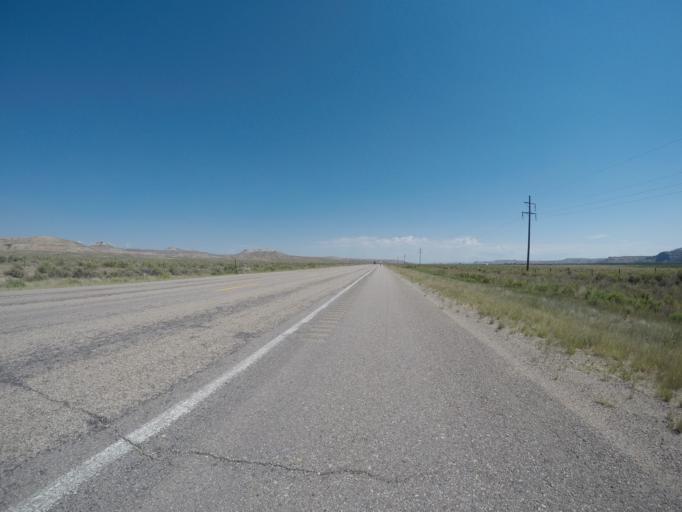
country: US
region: Wyoming
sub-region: Sublette County
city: Marbleton
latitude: 42.3476
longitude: -110.1614
